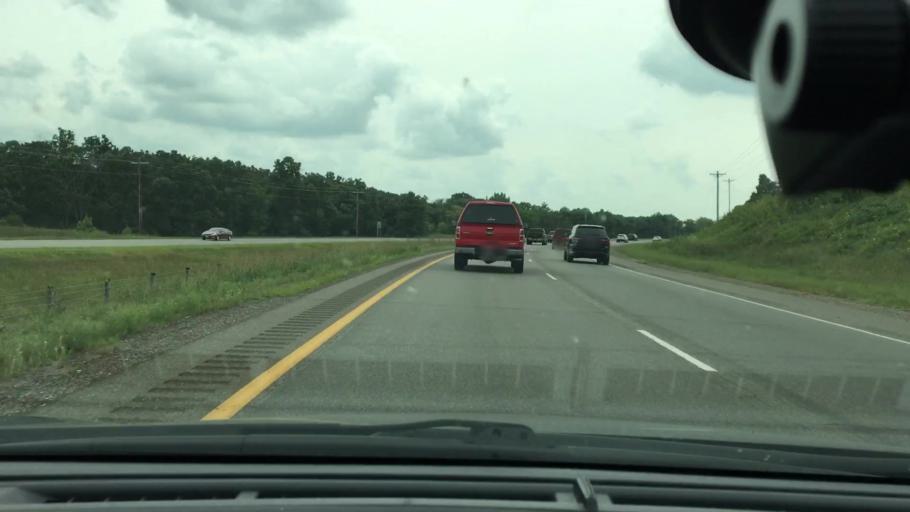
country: US
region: Minnesota
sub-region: Sherburne County
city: Elk River
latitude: 45.3535
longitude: -93.5595
